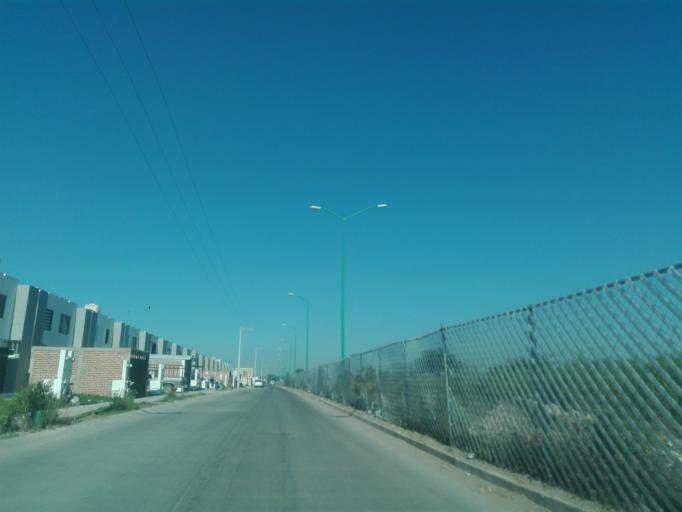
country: MX
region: Guanajuato
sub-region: Leon
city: Ladrilleras del Refugio
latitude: 21.0719
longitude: -101.5609
